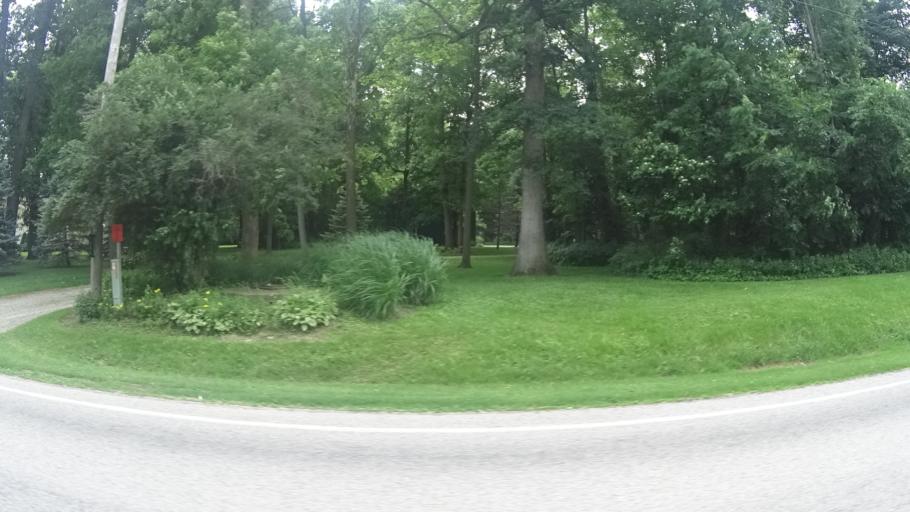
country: US
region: Ohio
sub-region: Erie County
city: Milan
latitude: 41.3226
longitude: -82.6347
